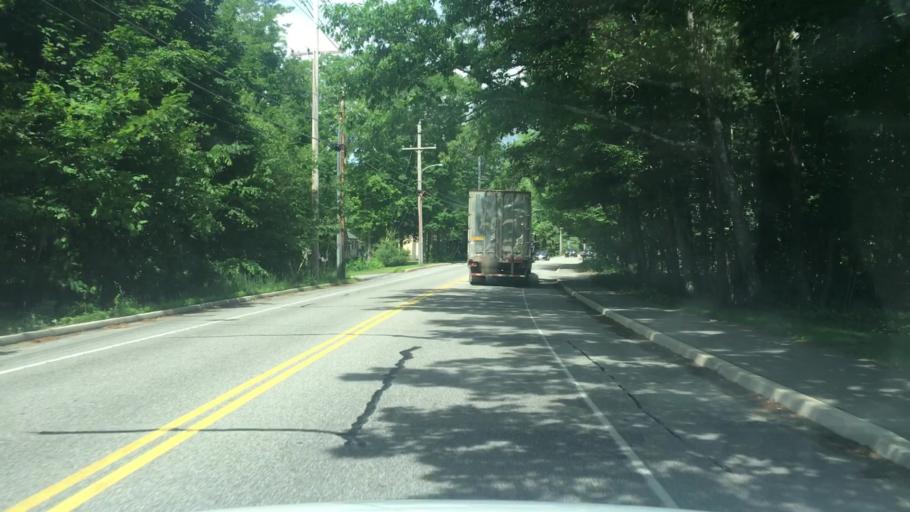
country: US
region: Maine
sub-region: York County
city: West Kennebunk
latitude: 43.4052
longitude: -70.5687
